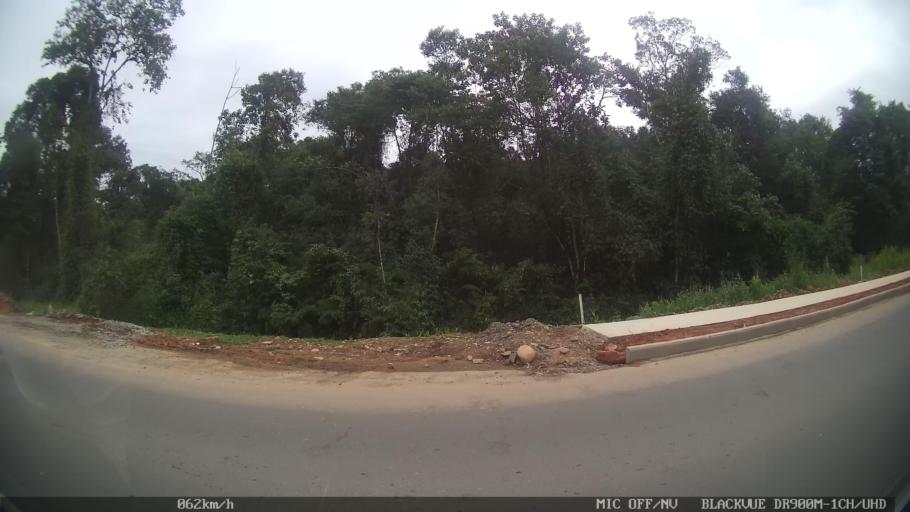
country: BR
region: Santa Catarina
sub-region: Joinville
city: Joinville
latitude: -26.2550
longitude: -48.8916
